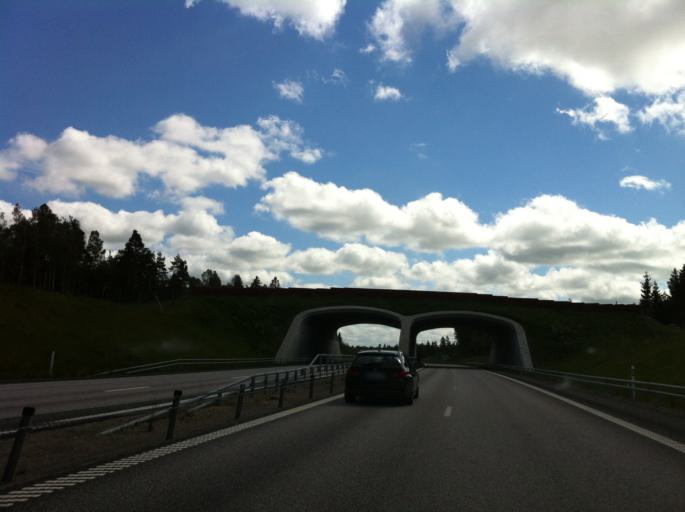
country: SE
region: Vaestra Goetaland
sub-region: Lilla Edets Kommun
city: Lodose
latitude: 58.0547
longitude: 12.1682
